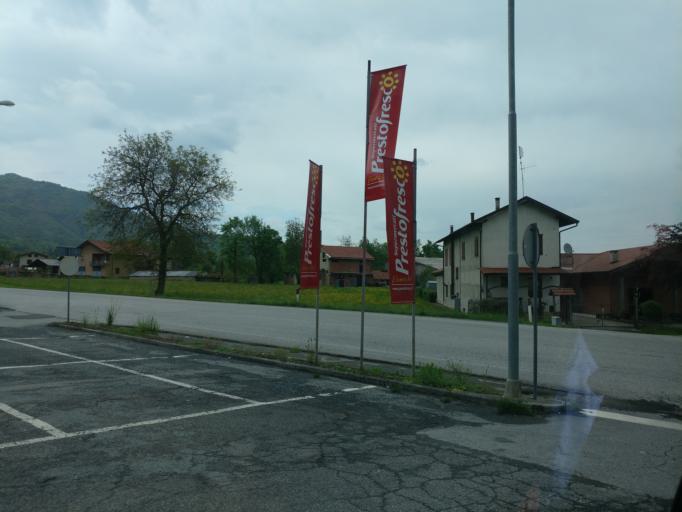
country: IT
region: Piedmont
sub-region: Provincia di Cuneo
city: Paesana
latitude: 44.6746
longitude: 7.2827
